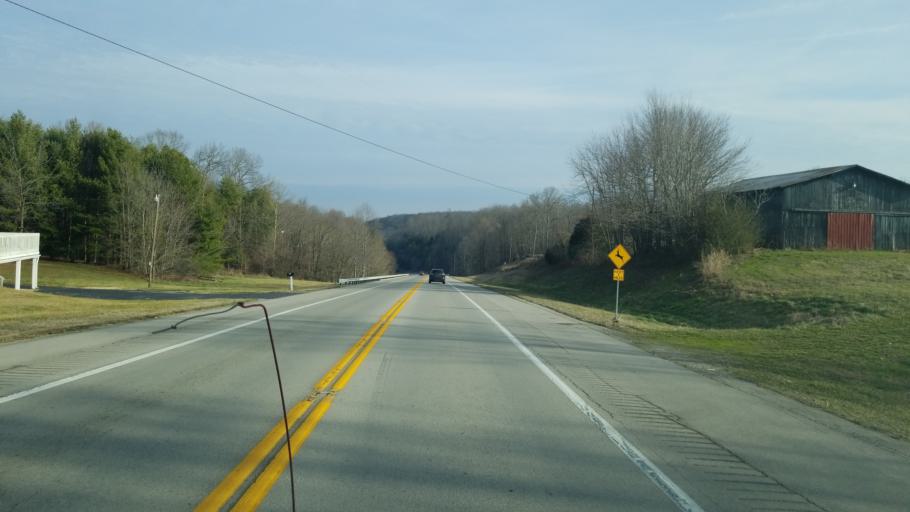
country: US
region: Kentucky
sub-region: Russell County
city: Russell Springs
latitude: 37.1447
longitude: -85.0300
